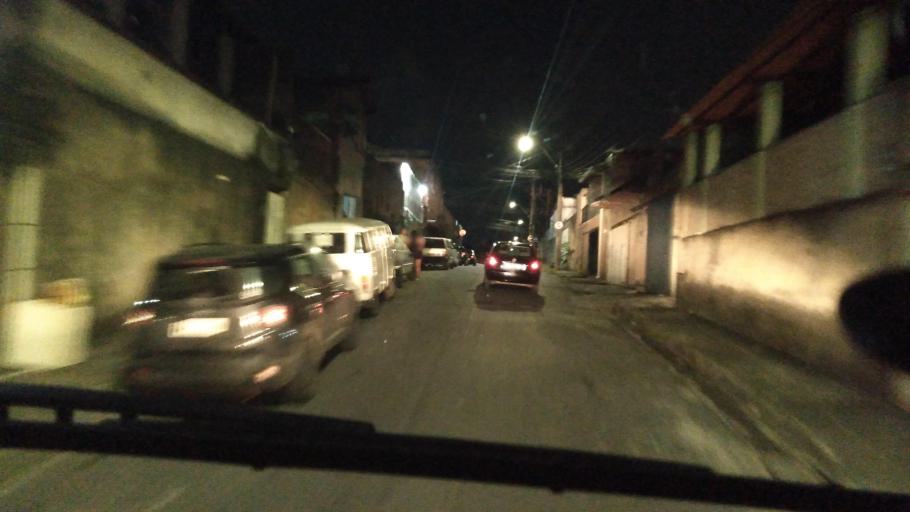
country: BR
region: Minas Gerais
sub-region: Belo Horizonte
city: Belo Horizonte
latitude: -19.9006
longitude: -43.9513
